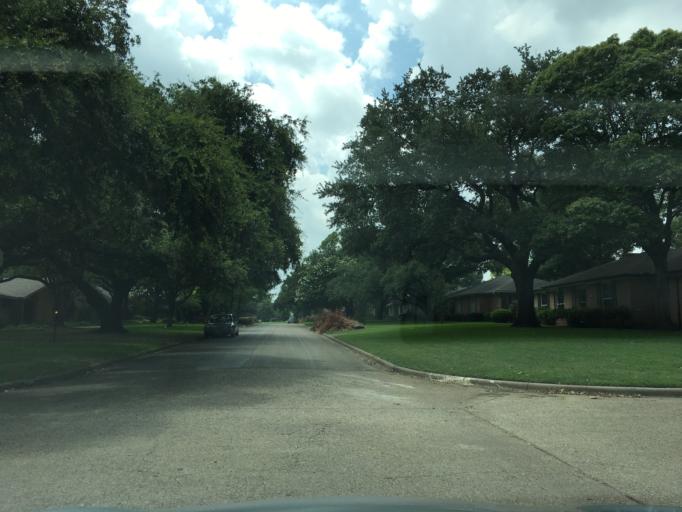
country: US
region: Texas
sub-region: Dallas County
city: University Park
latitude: 32.8957
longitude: -96.7825
